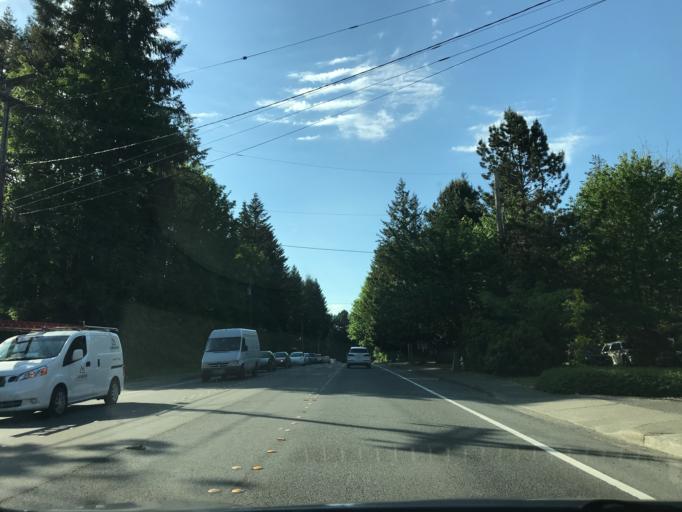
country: US
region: Washington
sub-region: King County
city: Issaquah
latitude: 47.5205
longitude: -122.0322
